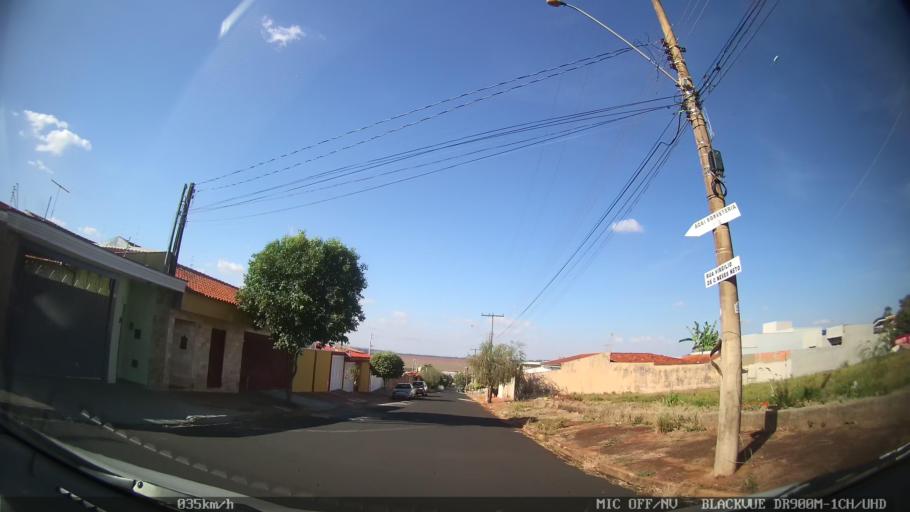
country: BR
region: Sao Paulo
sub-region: Ribeirao Preto
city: Ribeirao Preto
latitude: -21.1759
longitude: -47.7674
